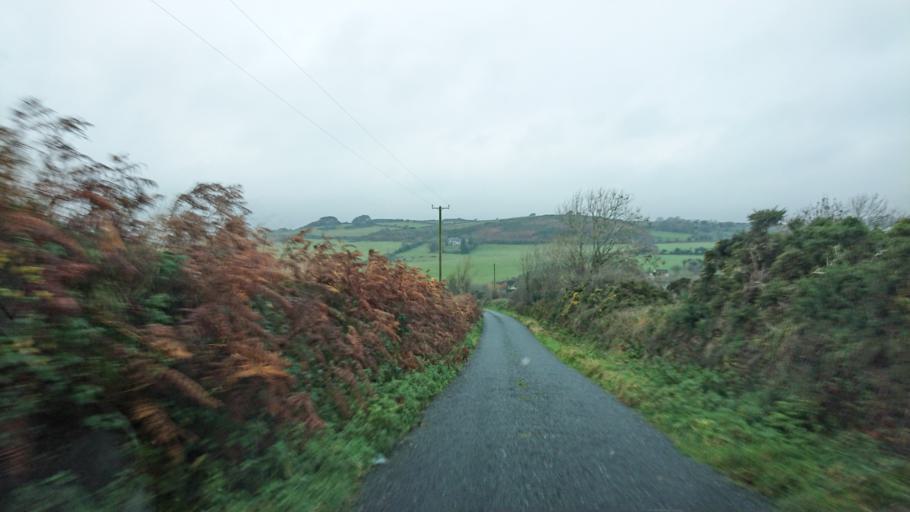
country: IE
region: Munster
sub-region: Waterford
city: Tra Mhor
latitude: 52.2000
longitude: -7.1708
